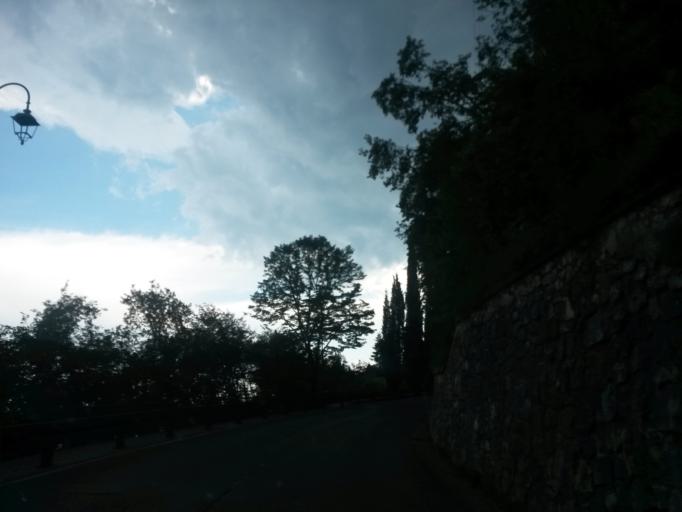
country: IT
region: Lombardy
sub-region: Provincia di Brescia
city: Gardola
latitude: 45.7404
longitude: 10.7288
